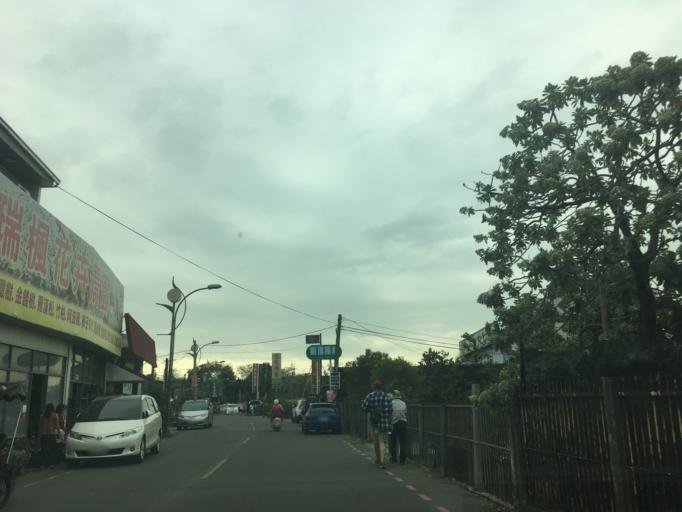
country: TW
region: Taiwan
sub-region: Nantou
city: Nantou
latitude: 23.9034
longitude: 120.5294
